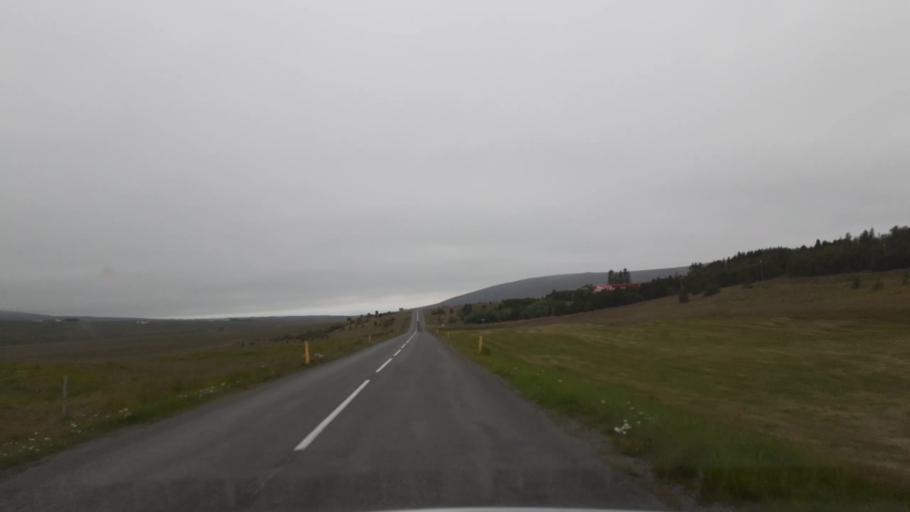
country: IS
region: Northeast
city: Siglufjoerdur
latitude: 65.7344
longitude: -19.1192
